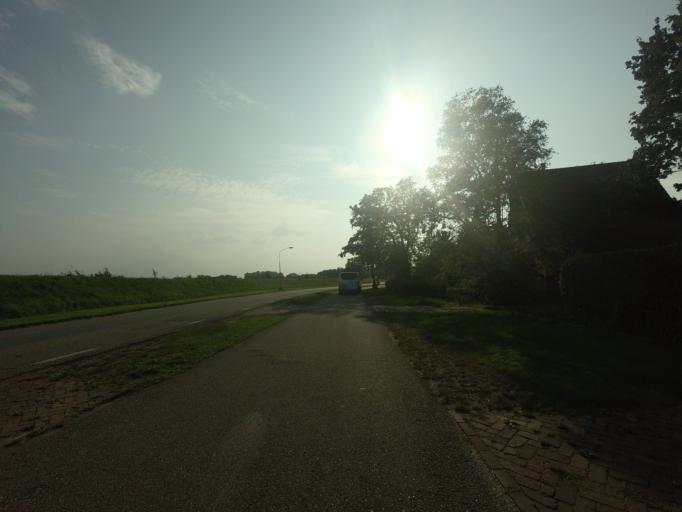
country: NL
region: Groningen
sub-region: Gemeente Haren
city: Haren
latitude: 53.1646
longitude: 6.5848
